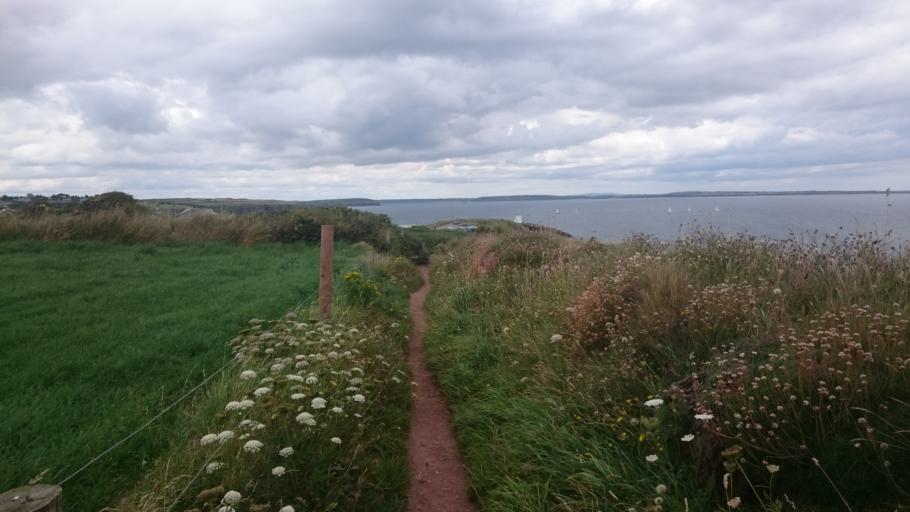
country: IE
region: Munster
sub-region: Waterford
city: Dunmore East
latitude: 52.1426
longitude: -6.9969
